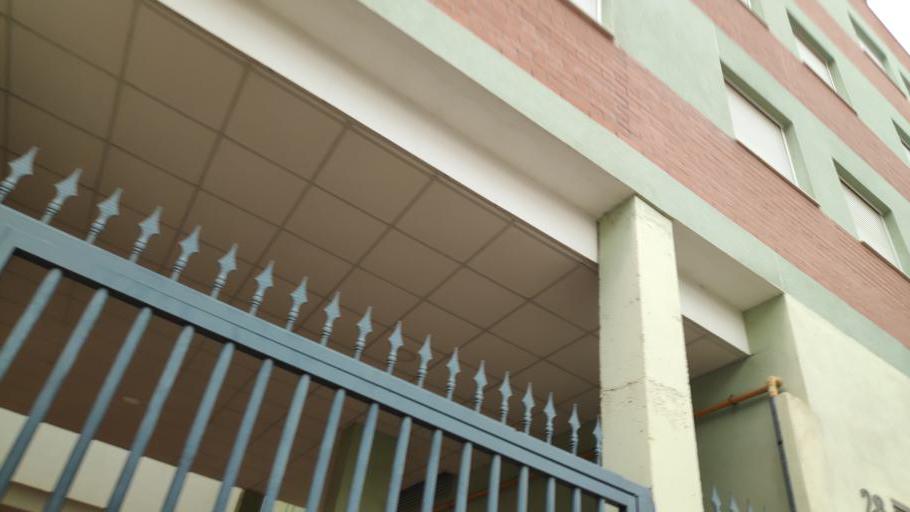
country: ES
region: Valencia
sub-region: Provincia de Castello
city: Castello de la Plana
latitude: 39.9908
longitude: -0.0650
